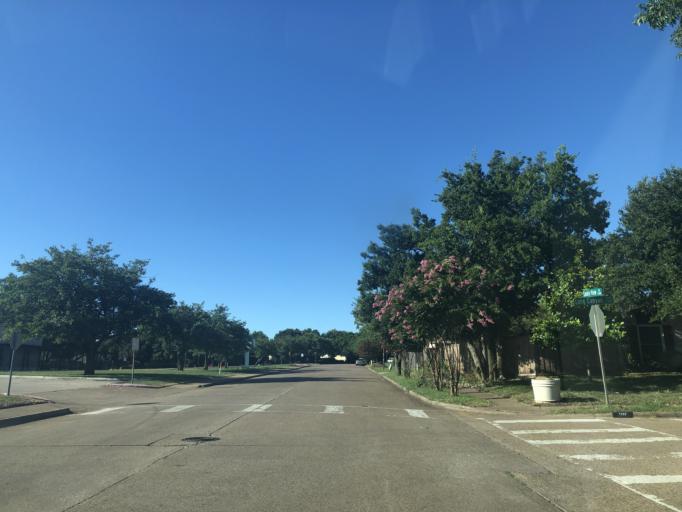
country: US
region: Texas
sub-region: Dallas County
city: Duncanville
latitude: 32.6413
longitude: -96.9480
